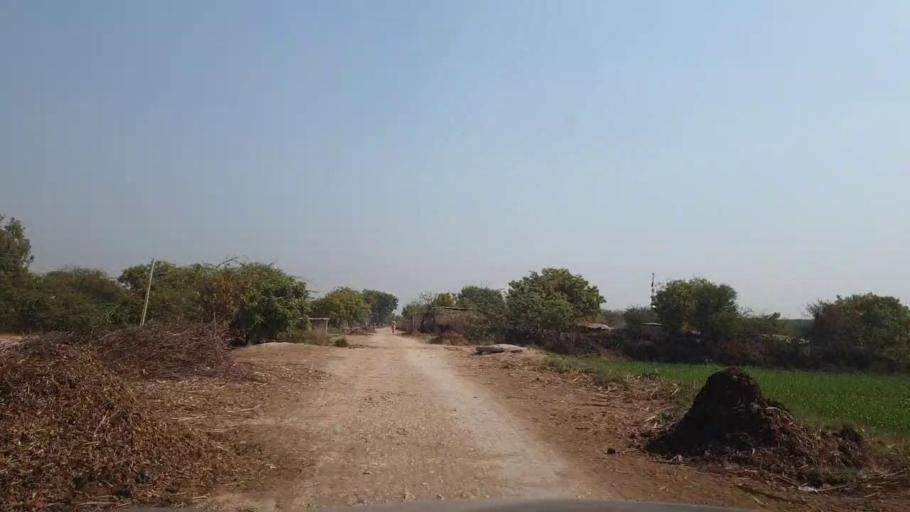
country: PK
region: Sindh
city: Tando Allahyar
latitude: 25.5500
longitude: 68.7193
